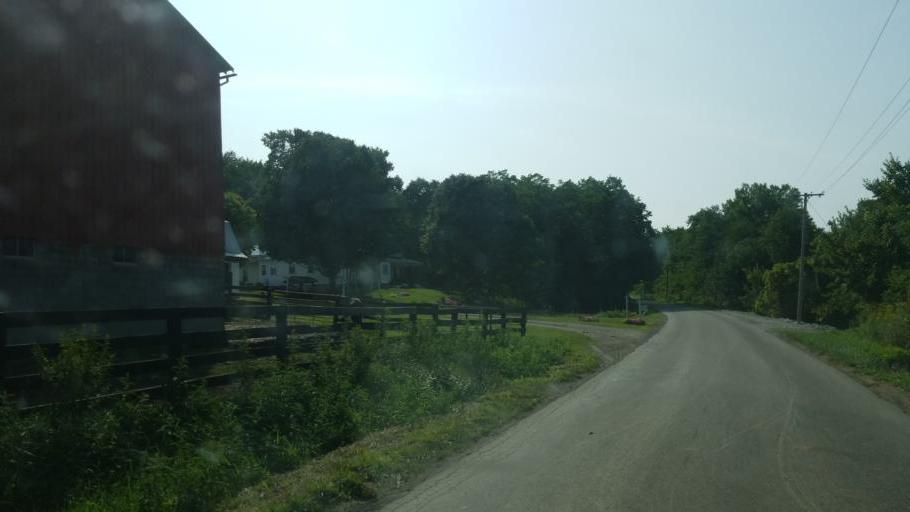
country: US
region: Ohio
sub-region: Knox County
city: Fredericktown
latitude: 40.5518
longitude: -82.6692
